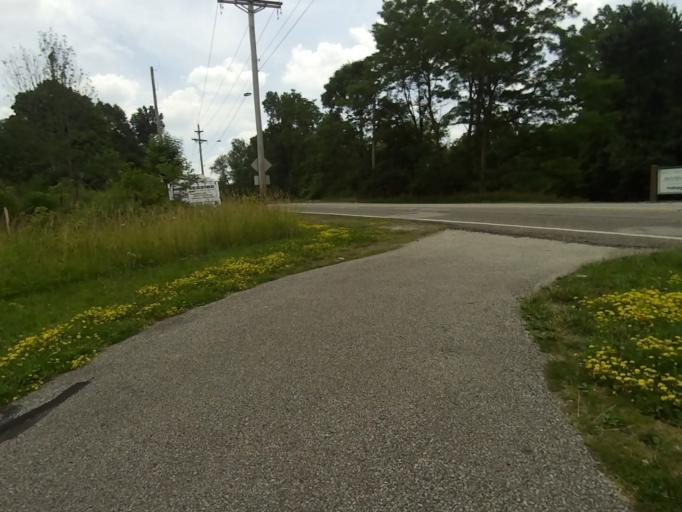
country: US
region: Ohio
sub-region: Summit County
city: Hudson
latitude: 41.2031
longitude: -81.4449
